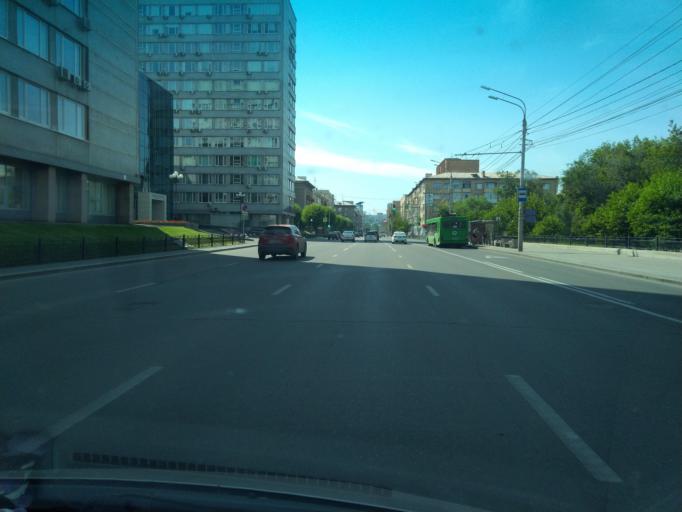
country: RU
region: Krasnoyarskiy
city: Krasnoyarsk
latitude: 56.0126
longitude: 92.8532
